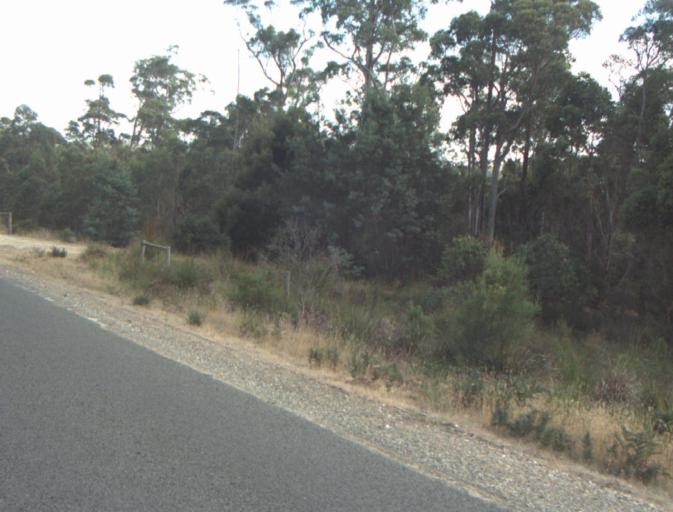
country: AU
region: Tasmania
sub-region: Dorset
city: Bridport
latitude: -41.1354
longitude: 147.2230
